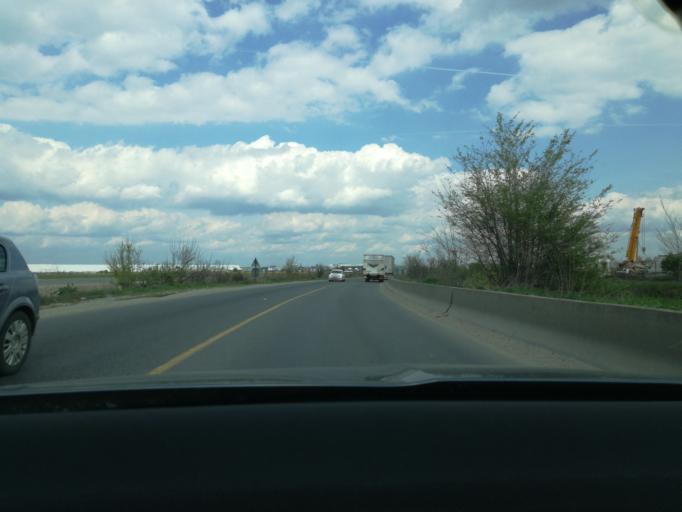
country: RO
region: Ilfov
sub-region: Comuna Chitila
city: Rudeni
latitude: 44.4824
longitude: 25.9727
